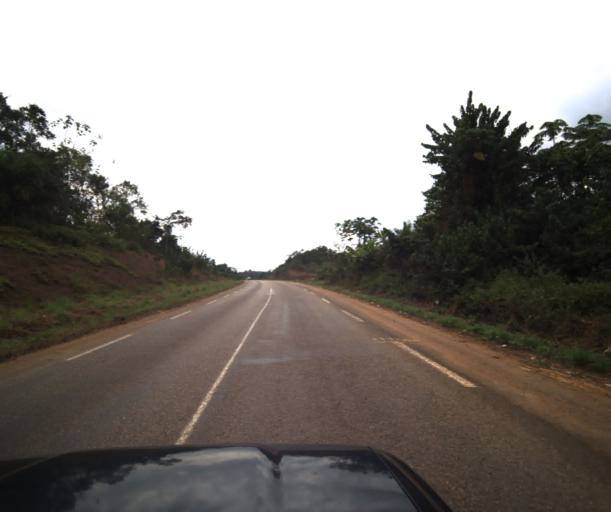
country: CM
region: Littoral
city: Edea
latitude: 3.8622
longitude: 10.0781
